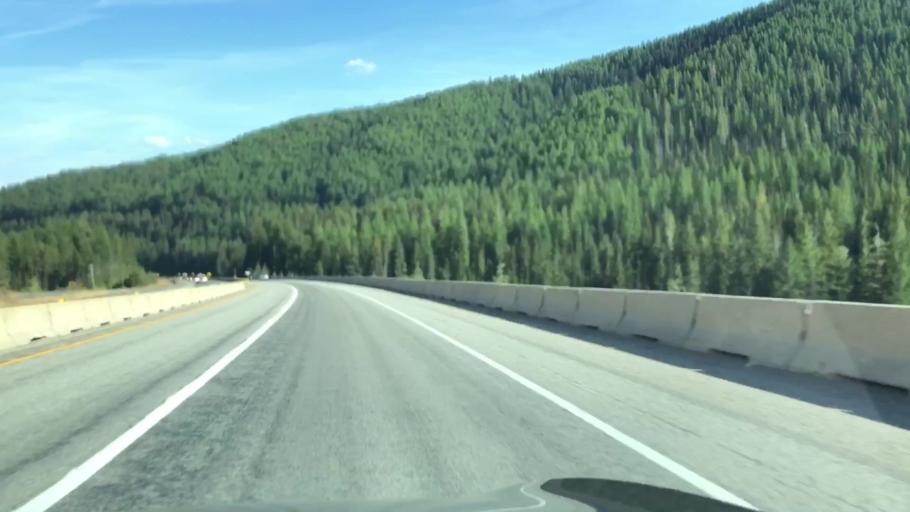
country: US
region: Idaho
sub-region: Shoshone County
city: Wallace
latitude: 47.4370
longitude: -115.6805
